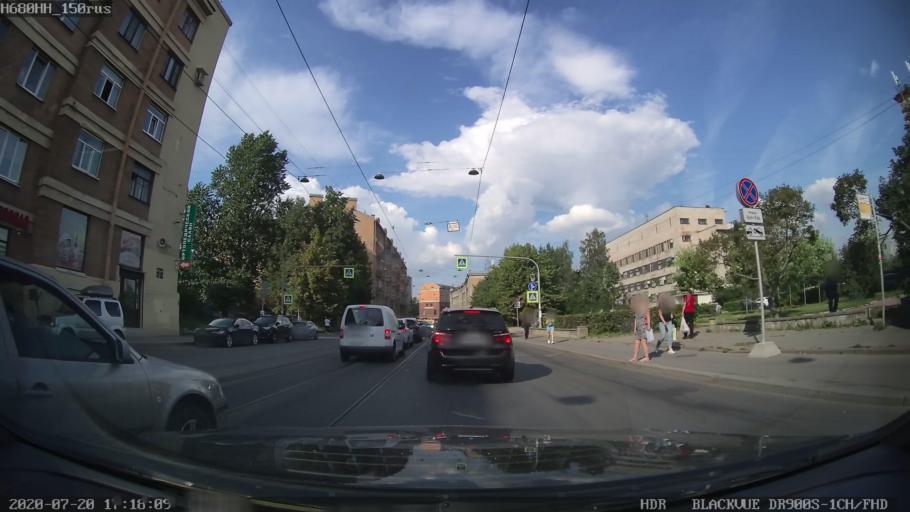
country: RU
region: St.-Petersburg
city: Admiralteisky
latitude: 59.9023
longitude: 30.2756
